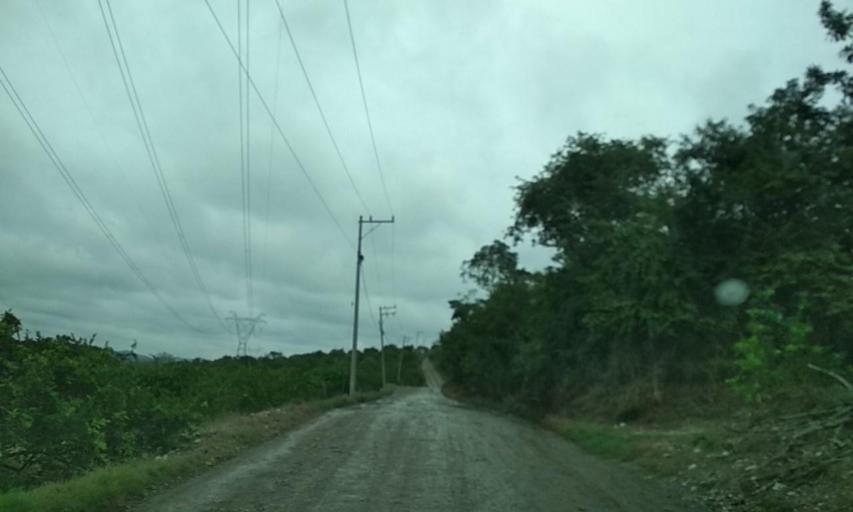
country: MX
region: Puebla
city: Espinal
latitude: 20.3126
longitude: -97.4152
